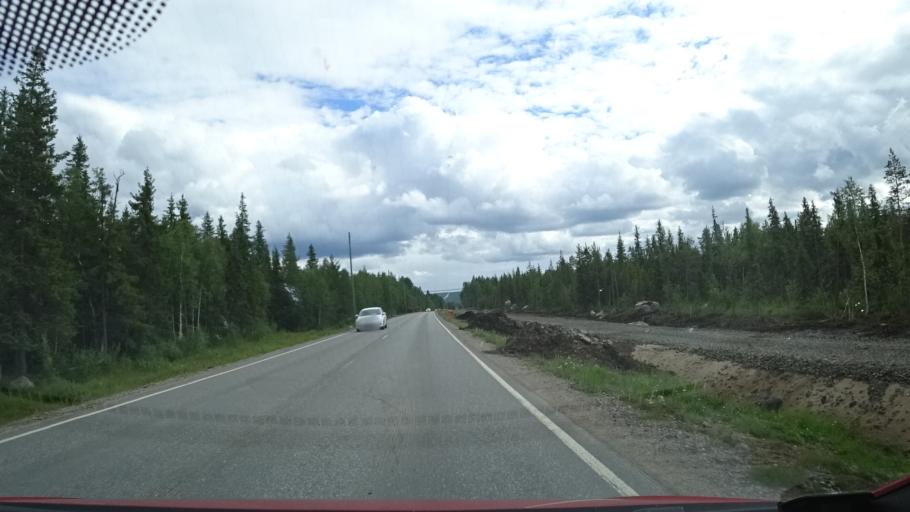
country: FI
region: Lapland
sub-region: Rovaniemi
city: Rovaniemi
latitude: 66.5354
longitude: 25.7288
